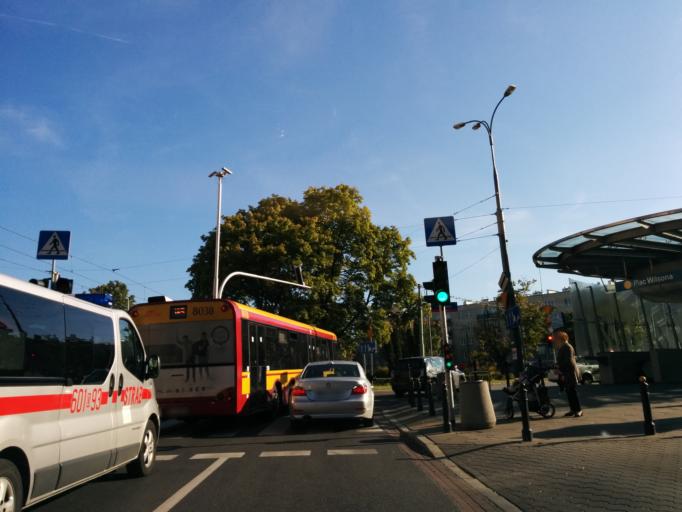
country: PL
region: Masovian Voivodeship
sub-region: Warszawa
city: Zoliborz
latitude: 52.2696
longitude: 20.9856
